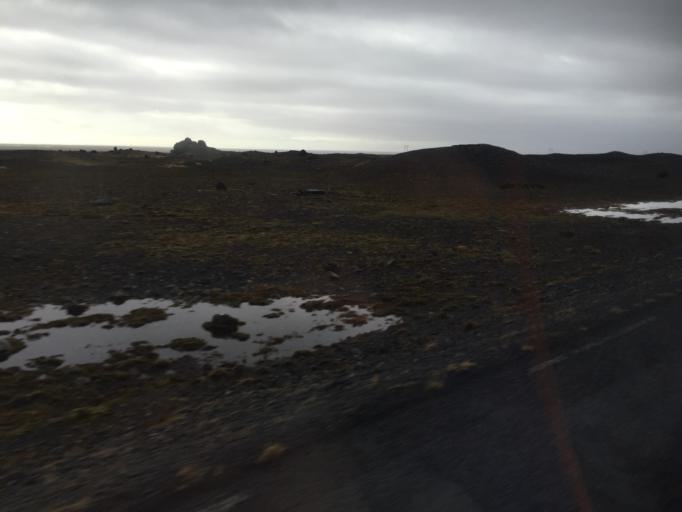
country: IS
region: East
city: Hoefn
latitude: 63.9177
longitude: -16.7646
